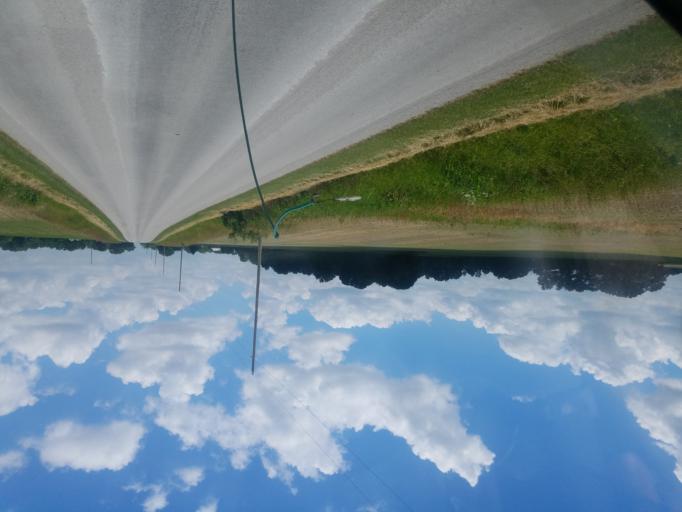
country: US
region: Ohio
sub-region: Huron County
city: Willard
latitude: 41.0791
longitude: -82.7056
